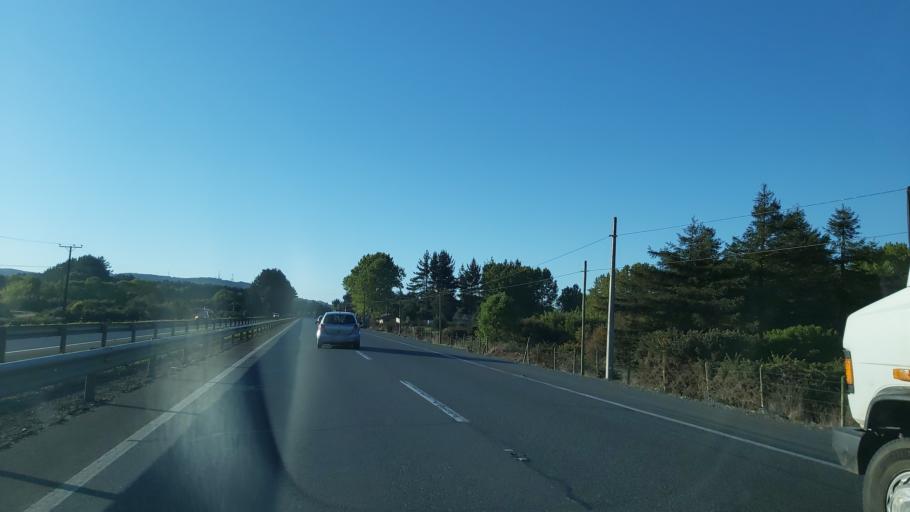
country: CL
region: Araucania
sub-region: Provincia de Malleco
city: Victoria
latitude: -38.1412
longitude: -72.3135
